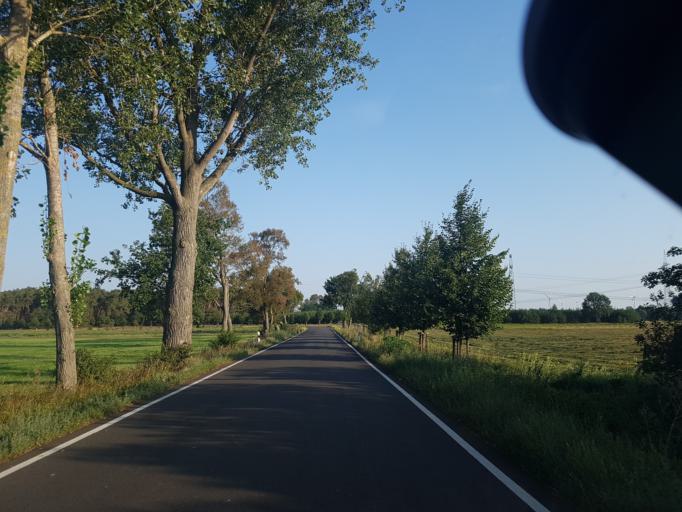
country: DE
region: Saxony-Anhalt
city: Holzdorf
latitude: 51.8253
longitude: 13.1409
